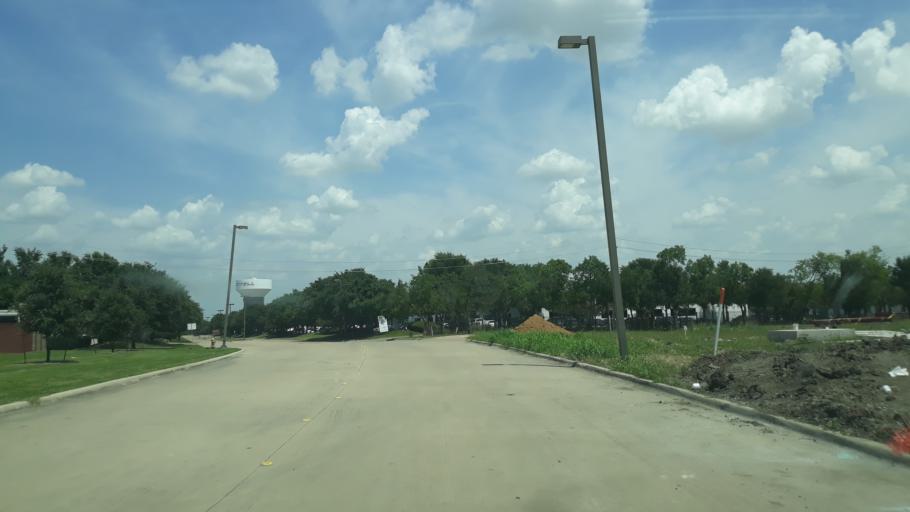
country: US
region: Texas
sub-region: Dallas County
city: Coppell
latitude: 32.9680
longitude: -97.0306
